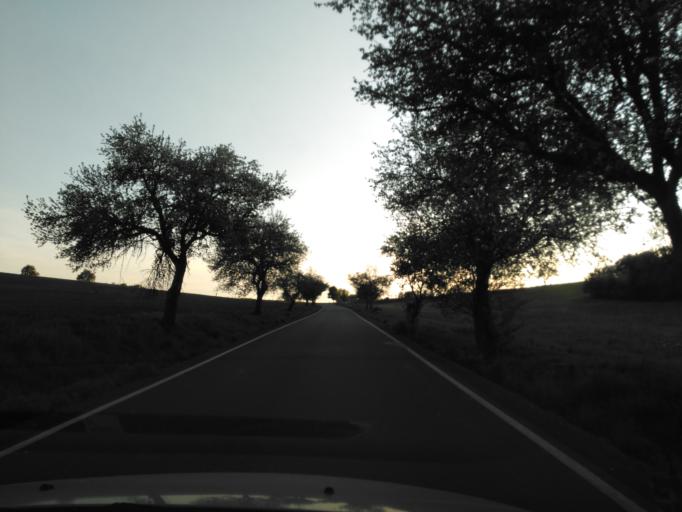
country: CZ
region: Central Bohemia
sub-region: Okres Beroun
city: Kraluv Dvur
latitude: 49.9167
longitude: 14.0338
